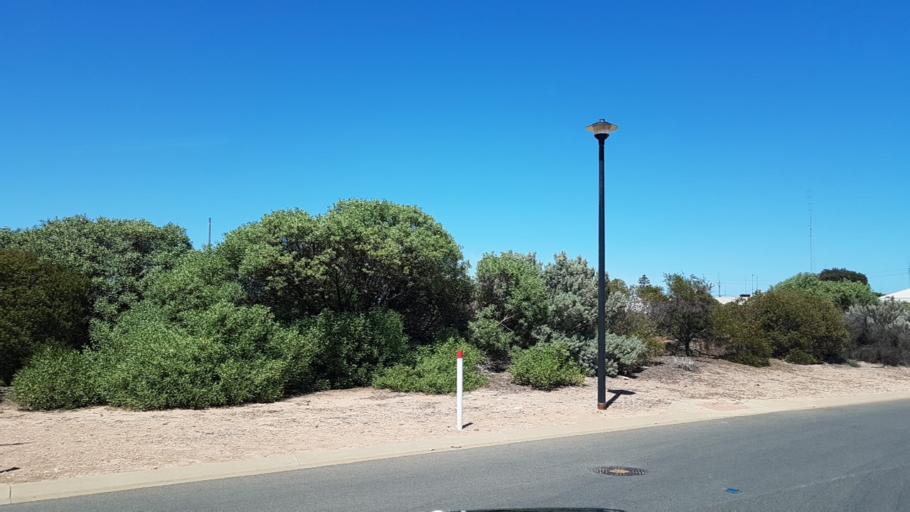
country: AU
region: South Australia
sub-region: Copper Coast
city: Wallaroo
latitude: -33.8947
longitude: 137.6304
